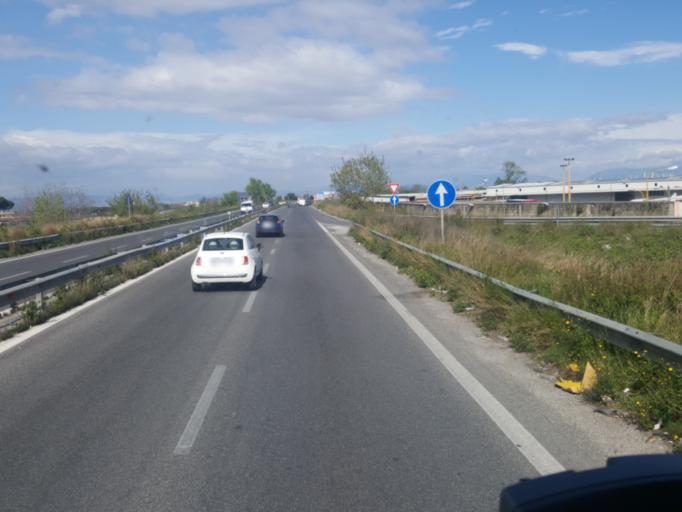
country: IT
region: Campania
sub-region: Provincia di Napoli
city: Qualiano
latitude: 40.9314
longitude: 14.1352
